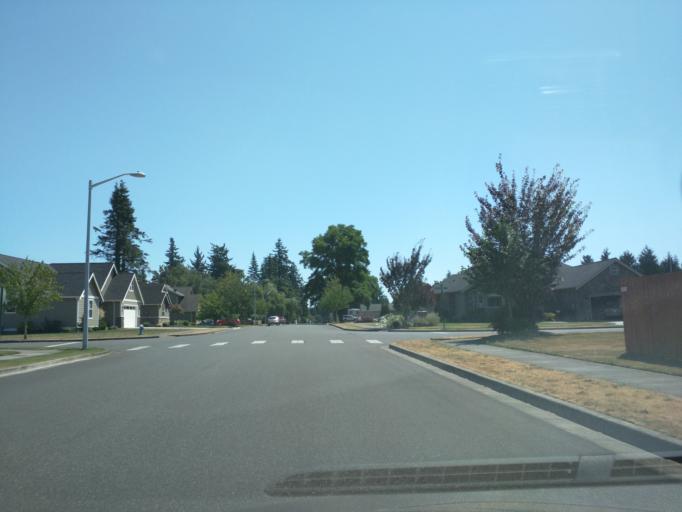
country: US
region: Washington
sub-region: Whatcom County
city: Lynden
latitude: 48.9512
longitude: -122.4605
